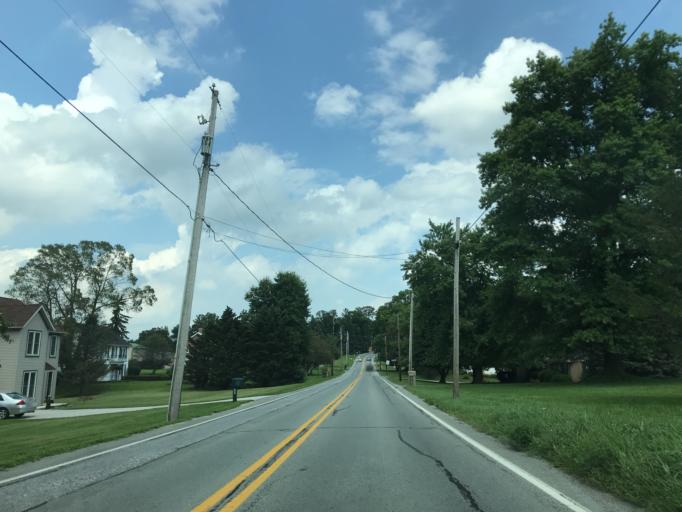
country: US
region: Pennsylvania
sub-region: York County
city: Red Lion
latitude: 39.8813
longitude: -76.6103
